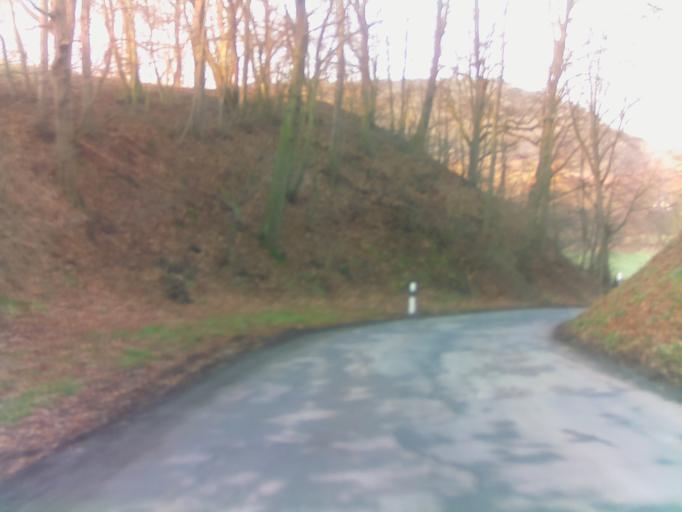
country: DE
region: Thuringia
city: Schops
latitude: 50.8305
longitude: 11.6032
